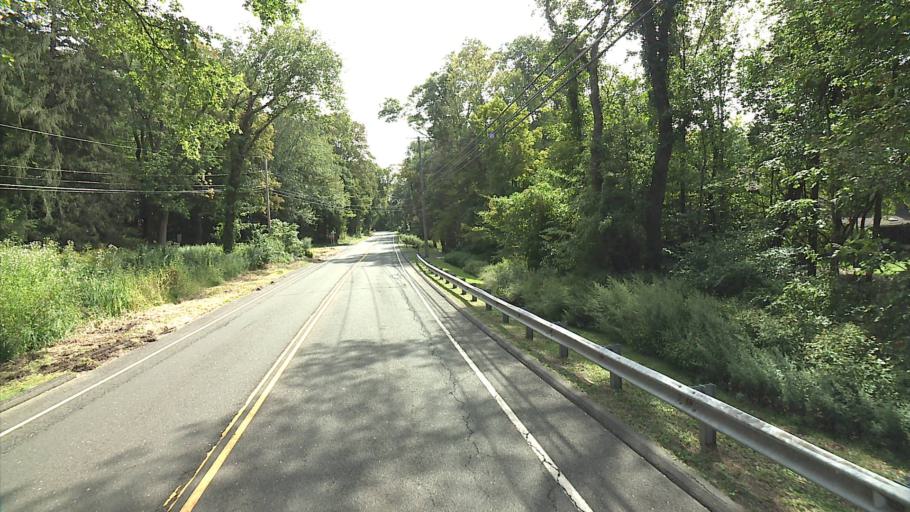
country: US
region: Connecticut
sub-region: Fairfield County
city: North Stamford
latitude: 41.1559
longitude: -73.5589
